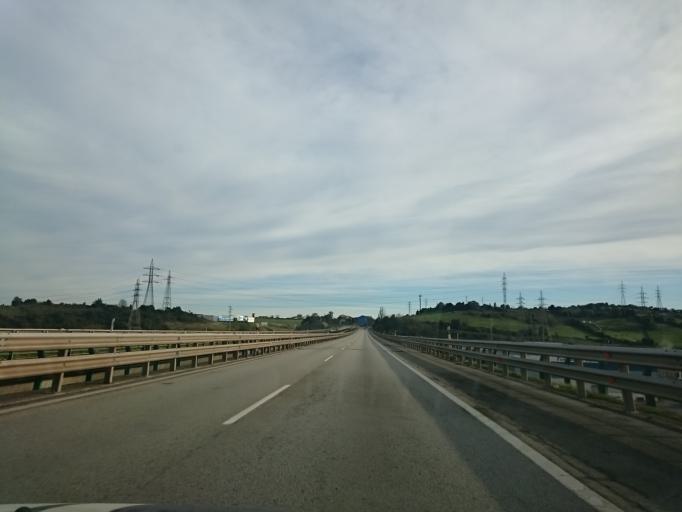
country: ES
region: Asturias
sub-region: Province of Asturias
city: Natahoyo
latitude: 43.5124
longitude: -5.7362
